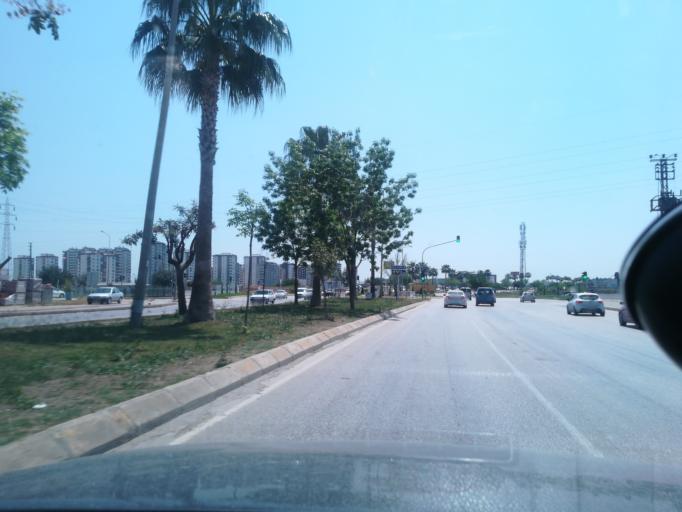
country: TR
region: Adana
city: Seyhan
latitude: 37.0061
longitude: 35.2515
